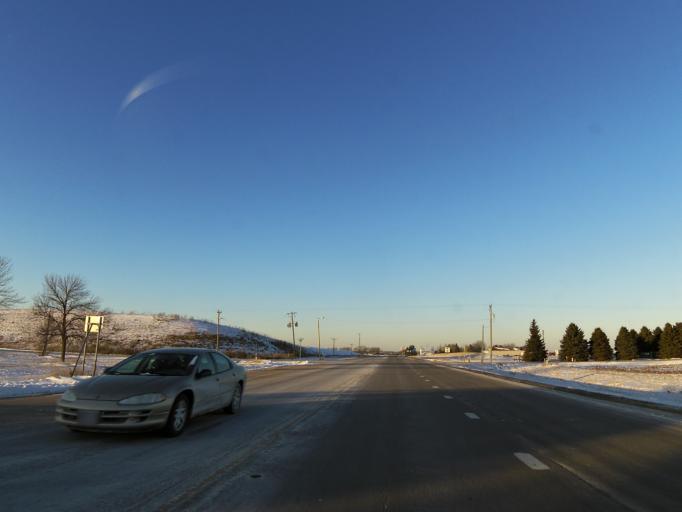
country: US
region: Minnesota
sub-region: Dakota County
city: Rosemount
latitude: 44.7021
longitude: -93.1365
